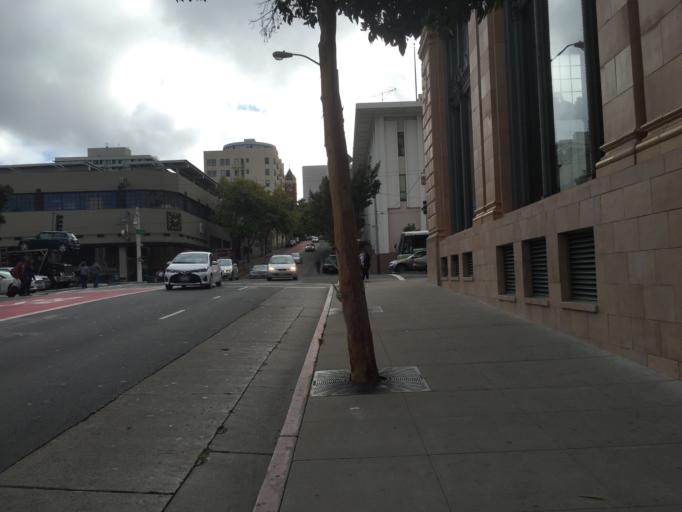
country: US
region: California
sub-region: San Francisco County
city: San Francisco
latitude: 37.7847
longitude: -122.4209
